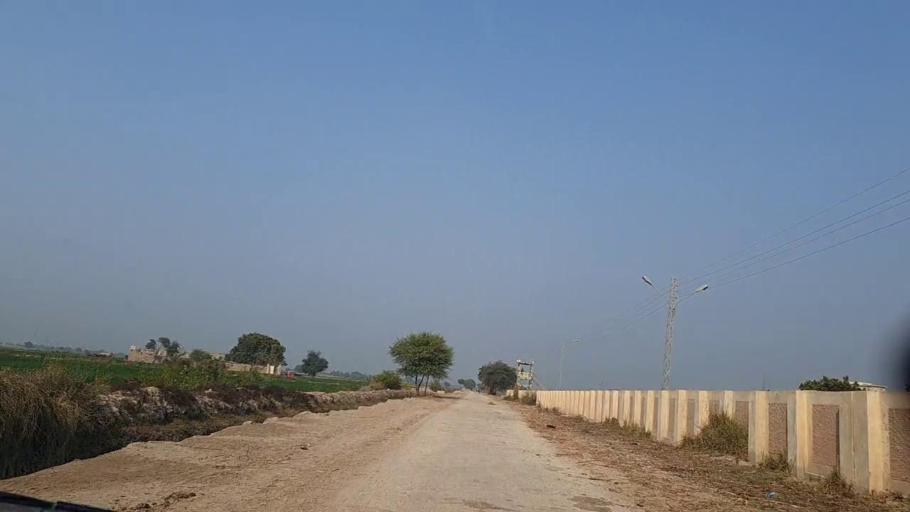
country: PK
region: Sindh
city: Sann
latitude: 26.1863
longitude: 68.1112
